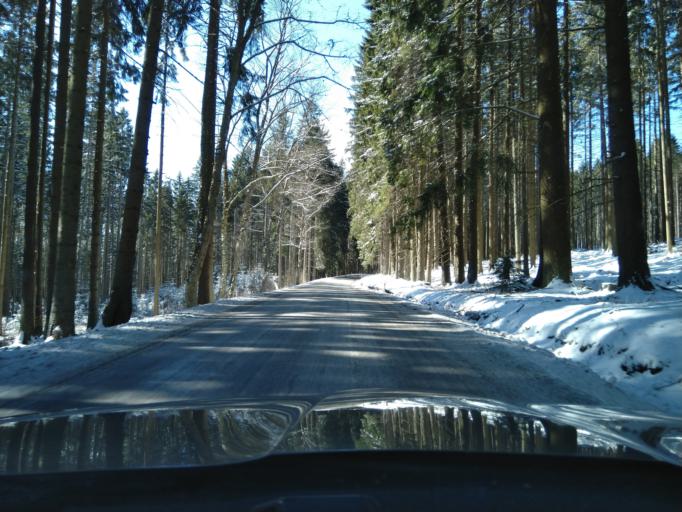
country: CZ
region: Jihocesky
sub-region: Okres Prachatice
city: Zdikov
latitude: 49.0508
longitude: 13.6895
